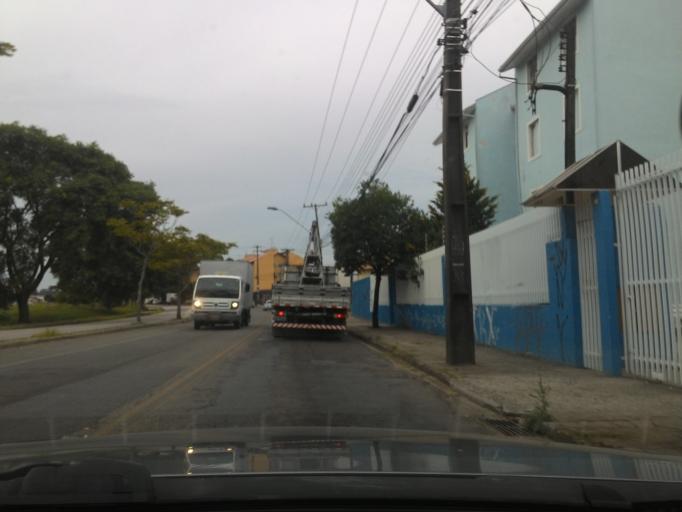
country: BR
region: Parana
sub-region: Pinhais
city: Pinhais
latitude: -25.4430
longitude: -49.2058
